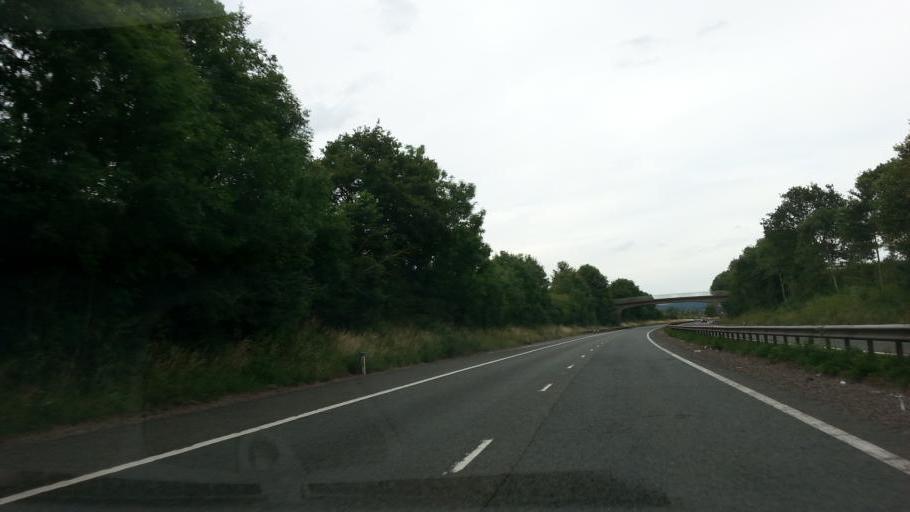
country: GB
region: England
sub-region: Herefordshire
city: Donnington
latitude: 51.9794
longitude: -2.4111
